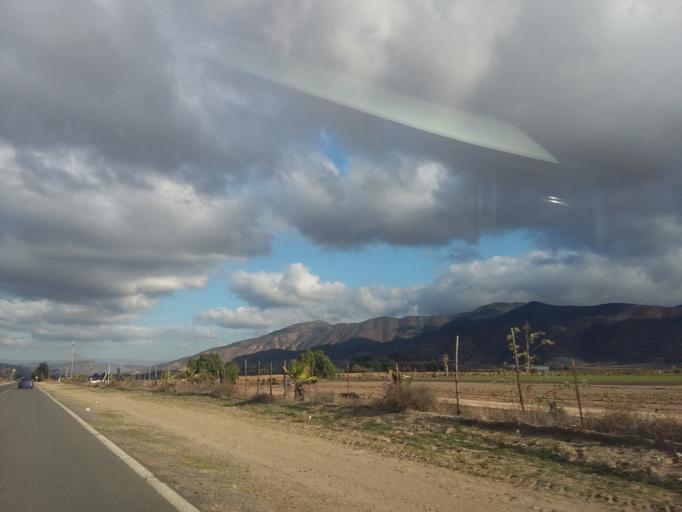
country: MX
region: Baja California
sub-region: Ensenada
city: Rancho Verde
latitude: 32.0824
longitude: -116.6069
